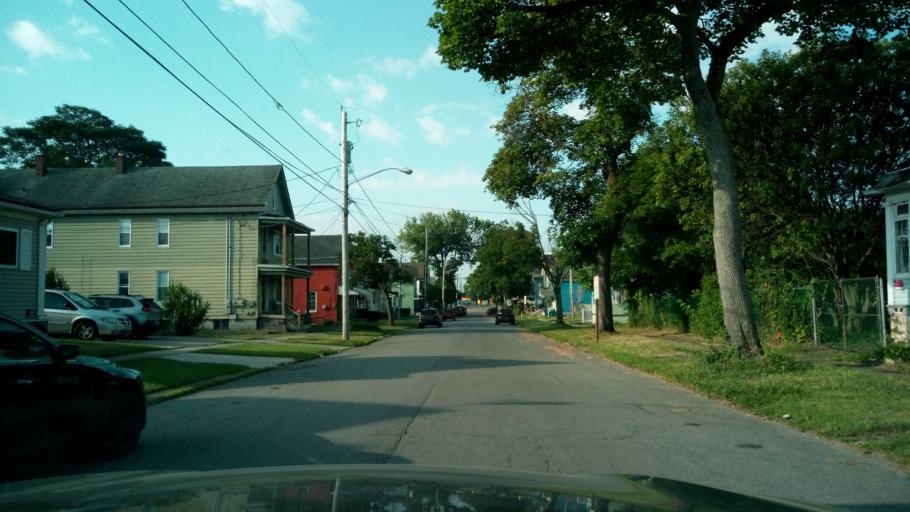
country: US
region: New York
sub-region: Erie County
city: Buffalo
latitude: 42.8963
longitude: -78.8623
